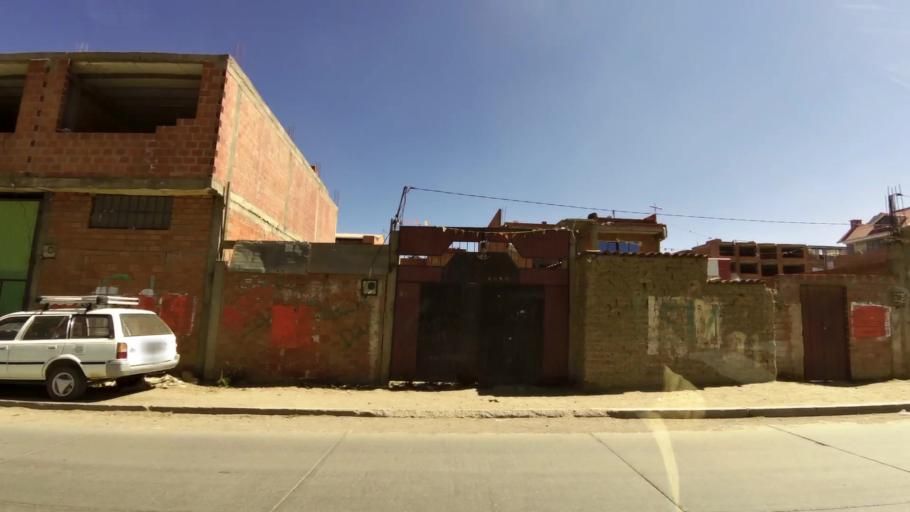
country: BO
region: La Paz
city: La Paz
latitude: -16.4974
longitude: -68.2068
